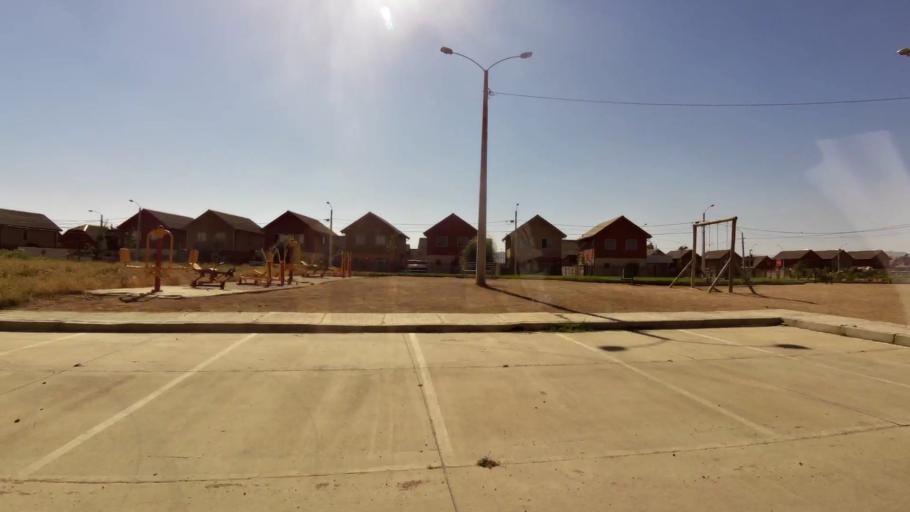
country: CL
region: Maule
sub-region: Provincia de Talca
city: Talca
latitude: -35.4149
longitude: -71.6110
